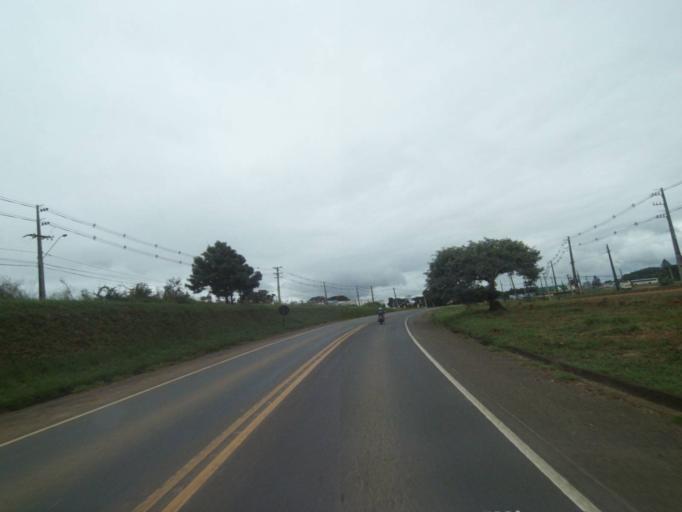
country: BR
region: Parana
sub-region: Telemaco Borba
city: Telemaco Borba
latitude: -24.3486
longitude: -50.6611
